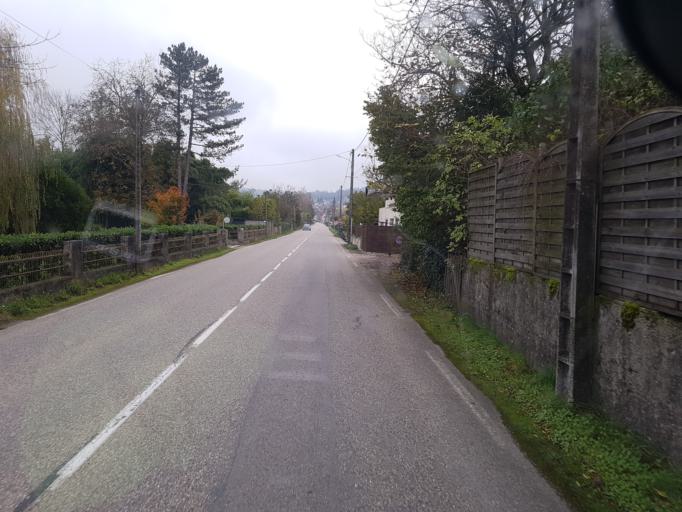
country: FR
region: Rhone-Alpes
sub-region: Departement de la Savoie
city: Saint-Genix-sur-Guiers
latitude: 45.5951
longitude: 5.6235
